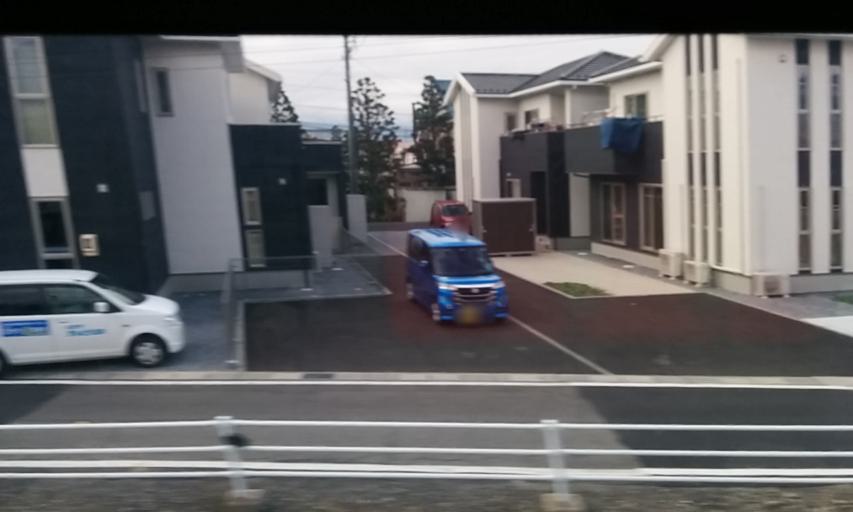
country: JP
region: Nagano
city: Matsumoto
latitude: 36.1885
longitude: 137.9614
